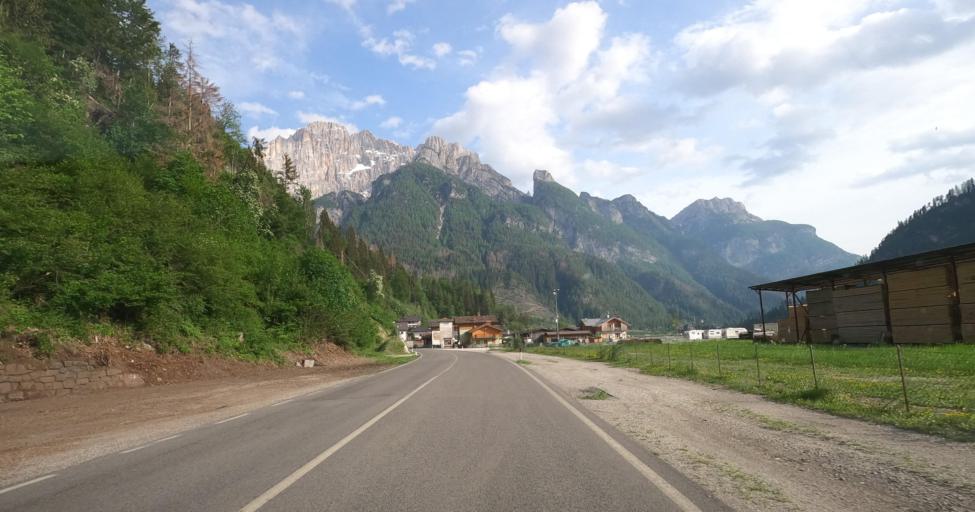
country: IT
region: Veneto
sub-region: Provincia di Belluno
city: Alleghe
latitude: 46.4135
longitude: 12.0161
